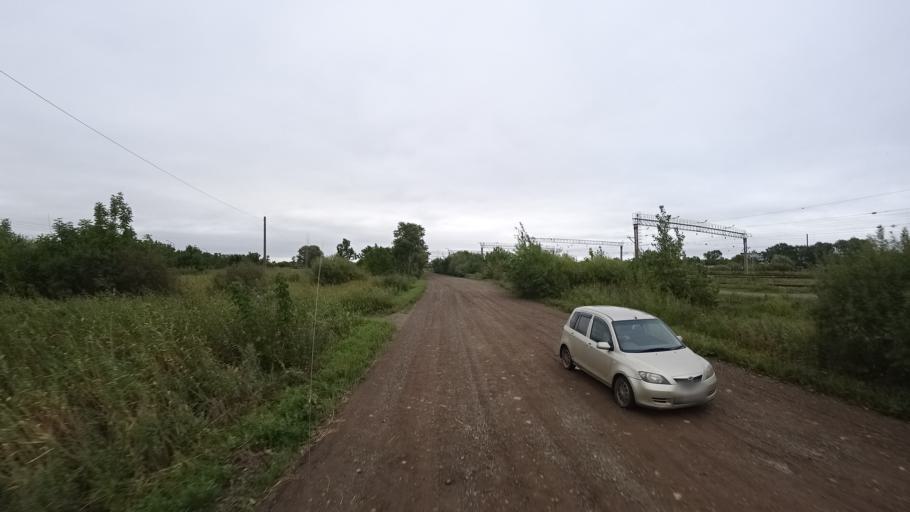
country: RU
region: Primorskiy
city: Chernigovka
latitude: 44.3372
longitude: 132.5278
